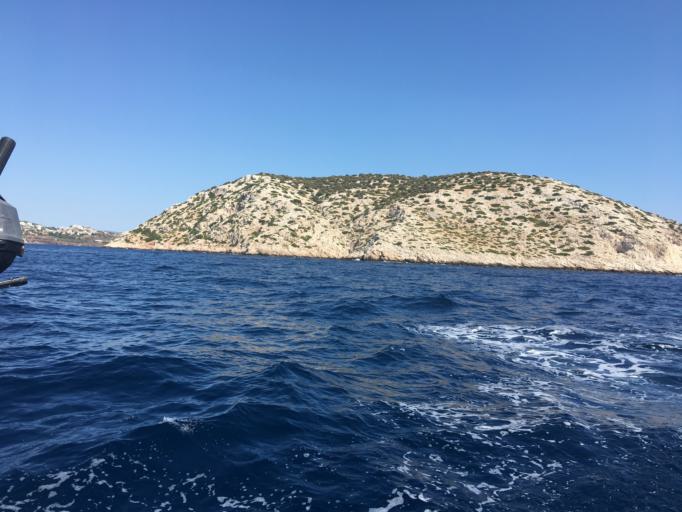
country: GR
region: Attica
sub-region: Nomarchia Anatolikis Attikis
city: Saronida
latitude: 37.7102
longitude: 23.8895
